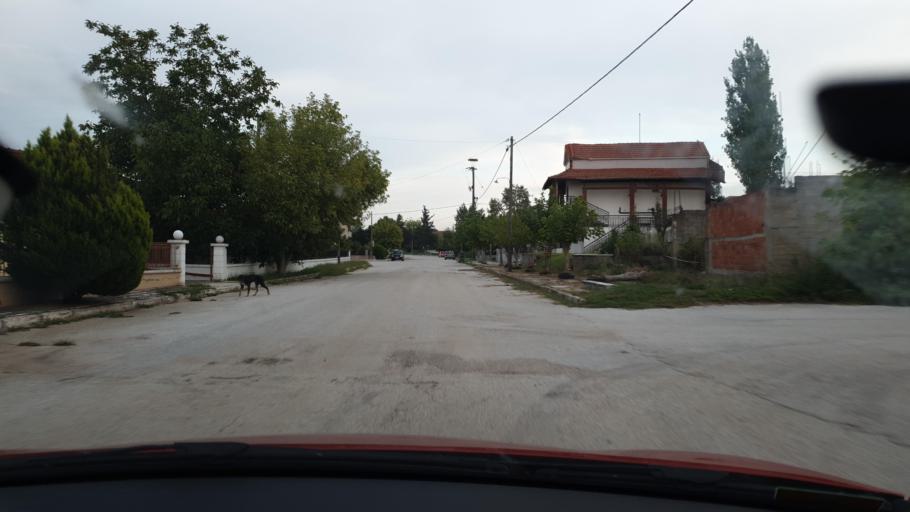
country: GR
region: Central Macedonia
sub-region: Nomos Kilkis
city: Kristoni
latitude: 40.9530
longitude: 22.8221
